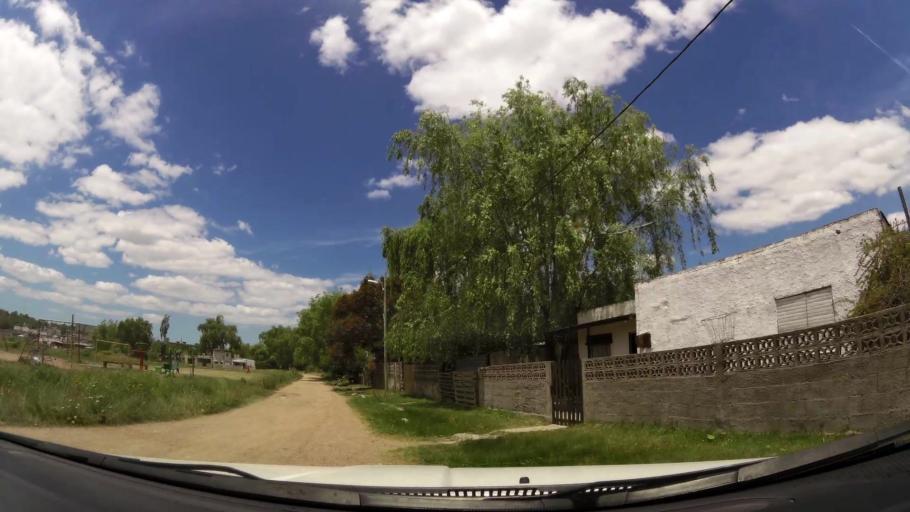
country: UY
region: Montevideo
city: Montevideo
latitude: -34.8649
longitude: -56.2473
